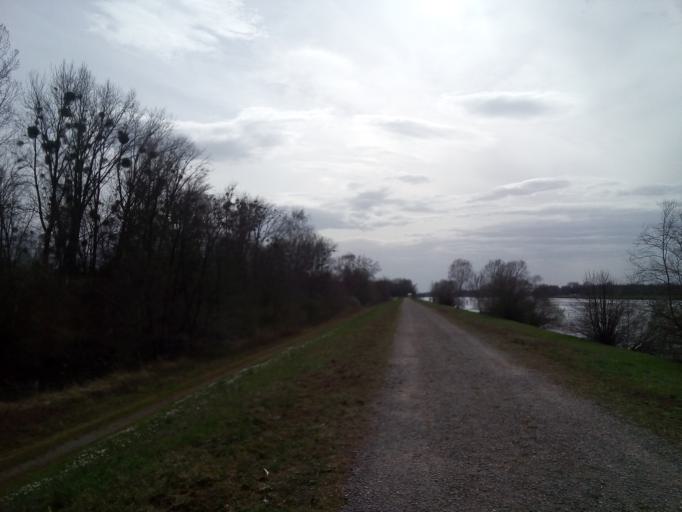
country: DE
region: Baden-Wuerttemberg
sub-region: Freiburg Region
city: Rheinau
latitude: 48.7121
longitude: 7.9542
